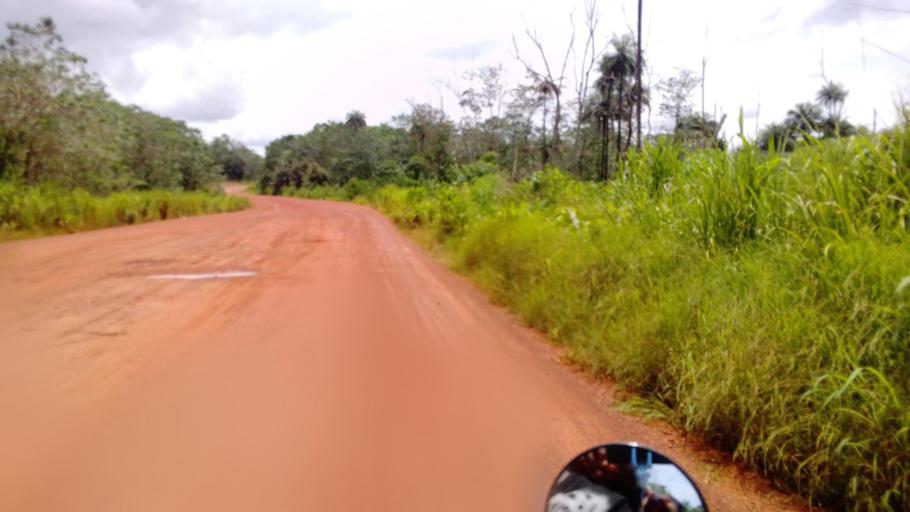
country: SL
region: Northern Province
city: Makeni
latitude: 9.0824
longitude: -12.1874
